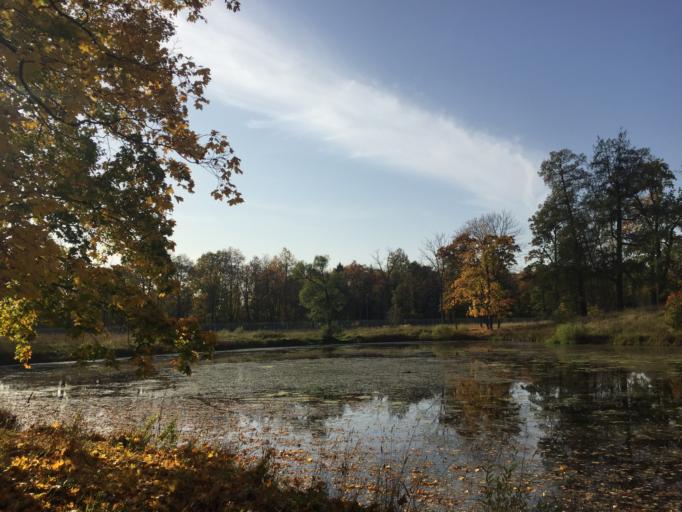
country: RU
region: St.-Petersburg
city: Pushkin
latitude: 59.7140
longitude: 30.3793
